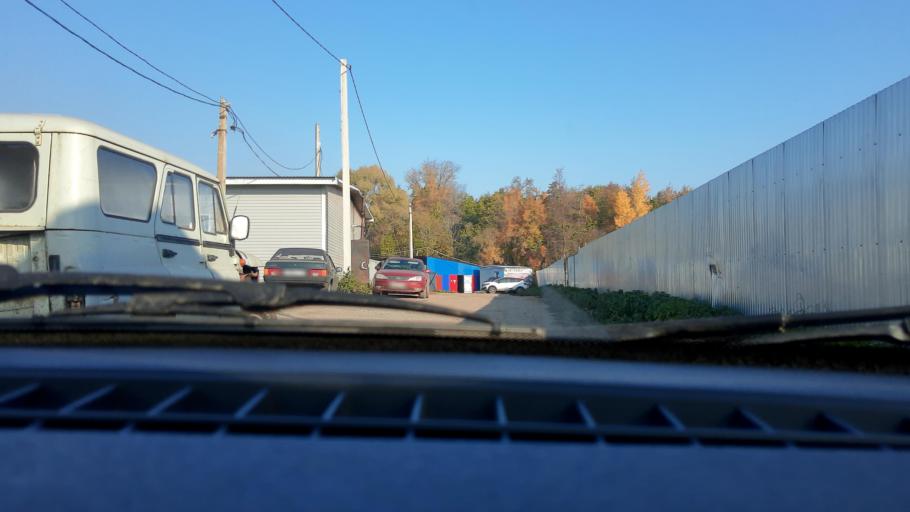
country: RU
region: Bashkortostan
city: Mikhaylovka
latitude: 54.8064
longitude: 55.8263
